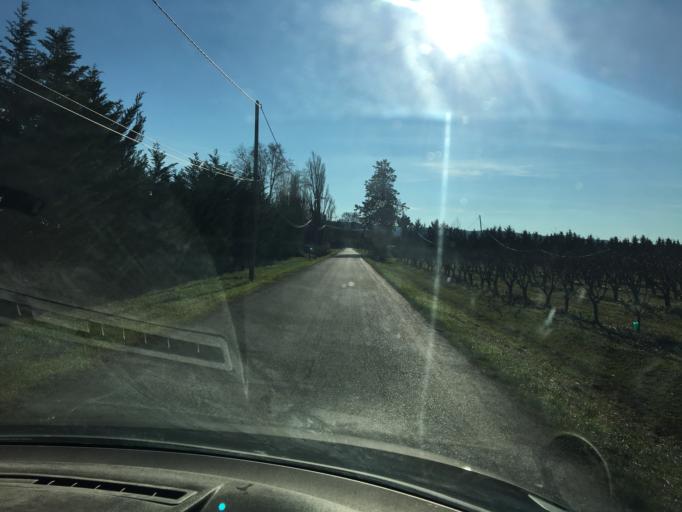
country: FR
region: Provence-Alpes-Cote d'Azur
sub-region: Departement des Bouches-du-Rhone
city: Maillane
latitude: 43.8120
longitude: 4.7874
